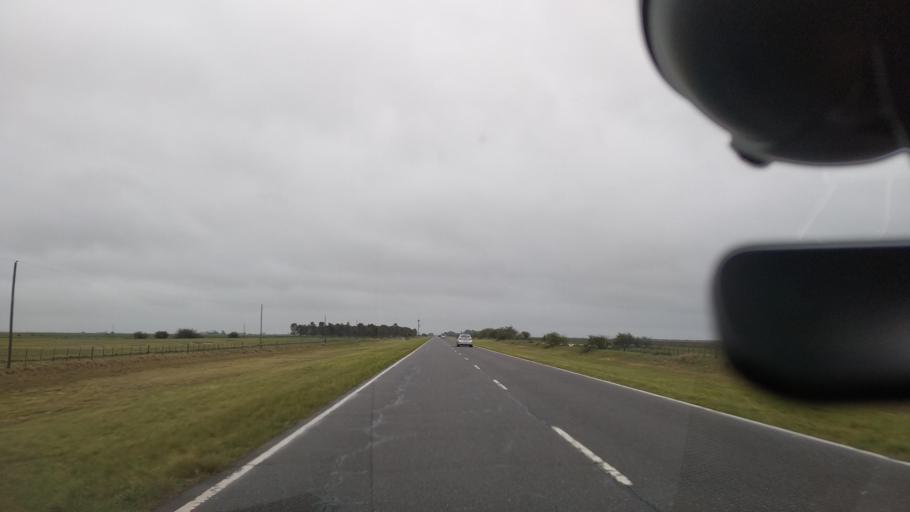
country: AR
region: Buenos Aires
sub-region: Partido de Dolores
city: Dolores
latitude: -36.0779
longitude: -57.4386
